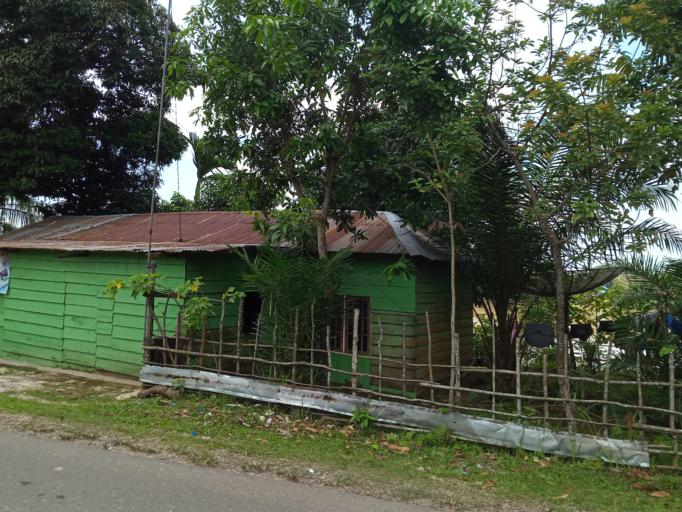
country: ID
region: Jambi
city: Mersam
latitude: -1.6466
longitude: 102.9725
